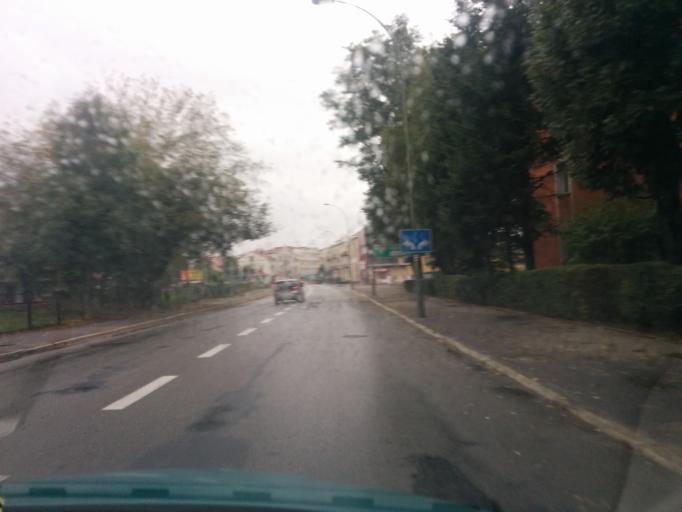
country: PL
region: Subcarpathian Voivodeship
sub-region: Powiat sanocki
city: Sanok
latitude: 49.5546
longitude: 22.2091
